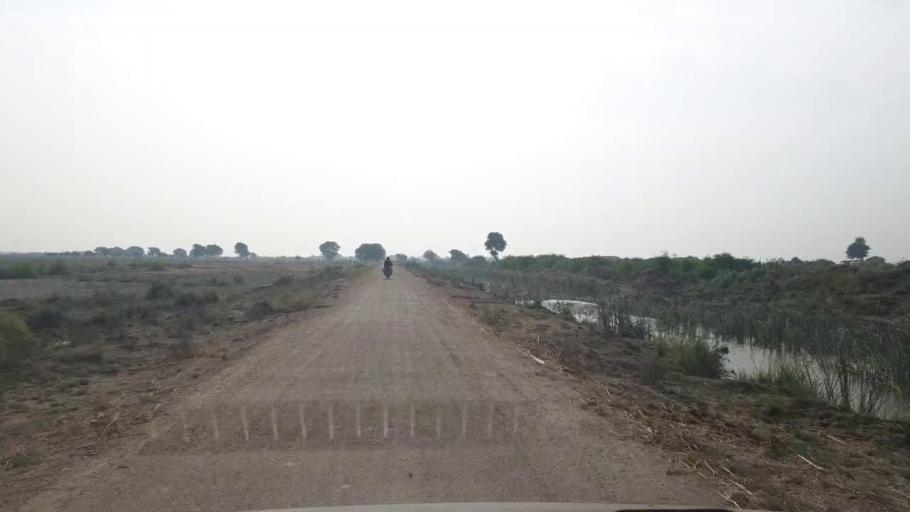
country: PK
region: Sindh
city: Tando Muhammad Khan
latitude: 25.1245
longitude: 68.4987
